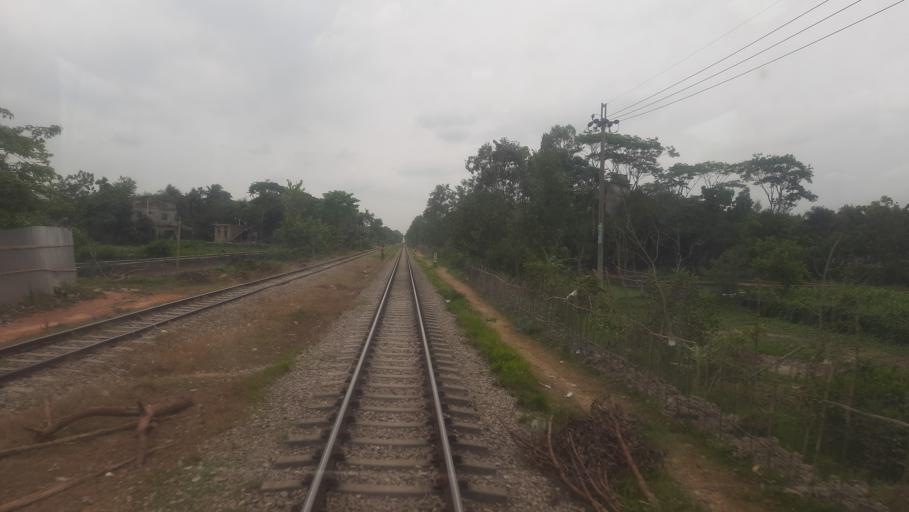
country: BD
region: Chittagong
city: Feni
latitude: 23.0229
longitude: 91.3900
